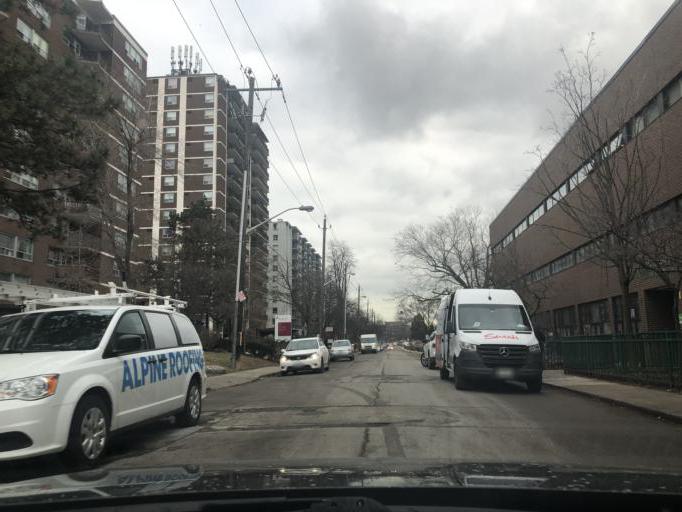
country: CA
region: Ontario
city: Toronto
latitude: 43.6876
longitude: -79.3520
